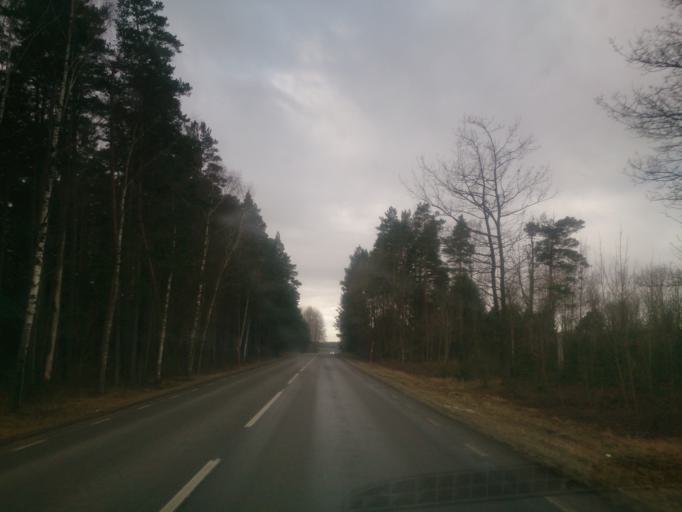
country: SE
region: OEstergoetland
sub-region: Linkopings Kommun
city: Ljungsbro
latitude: 58.4875
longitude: 15.4487
